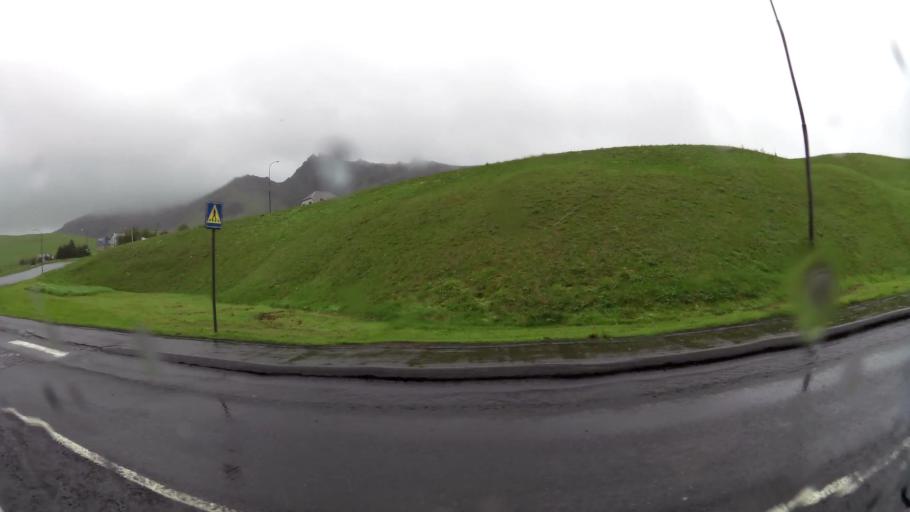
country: IS
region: South
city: Vestmannaeyjar
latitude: 63.4203
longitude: -19.0081
